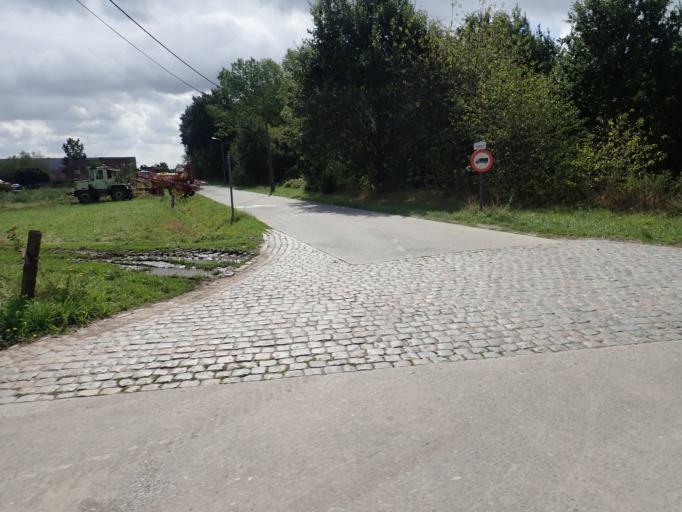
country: BE
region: Flanders
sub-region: Provincie Vlaams-Brabant
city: Londerzeel
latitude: 51.0319
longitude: 4.3187
